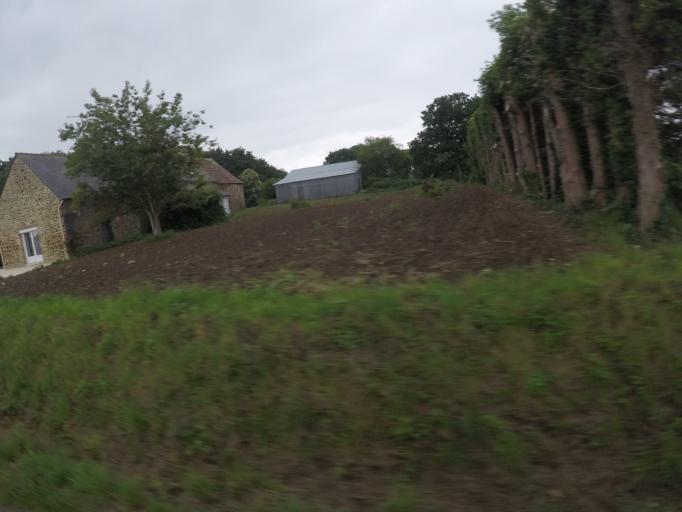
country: FR
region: Brittany
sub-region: Departement des Cotes-d'Armor
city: Goudelin
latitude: 48.6268
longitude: -3.0455
